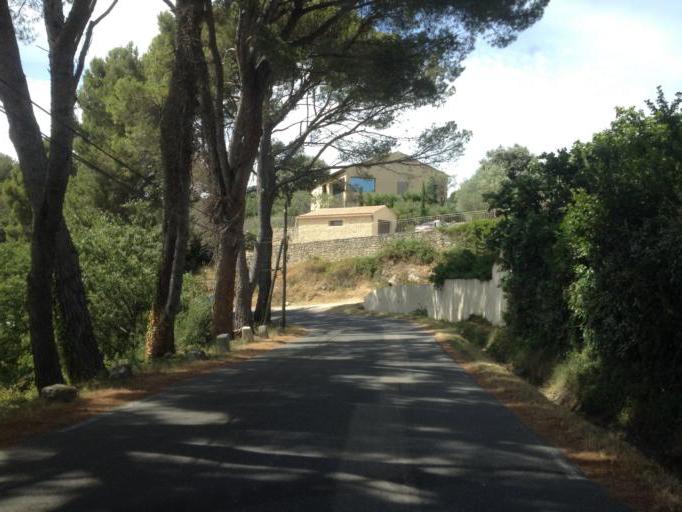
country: FR
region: Provence-Alpes-Cote d'Azur
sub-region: Departement du Vaucluse
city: Caromb
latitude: 44.1347
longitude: 5.0977
